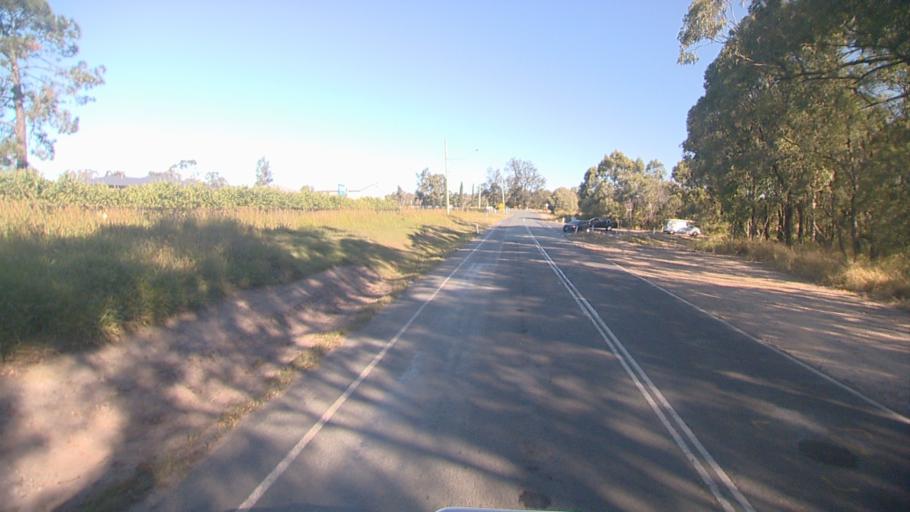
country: AU
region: Queensland
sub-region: Logan
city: Logan Reserve
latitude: -27.7499
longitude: 153.1311
